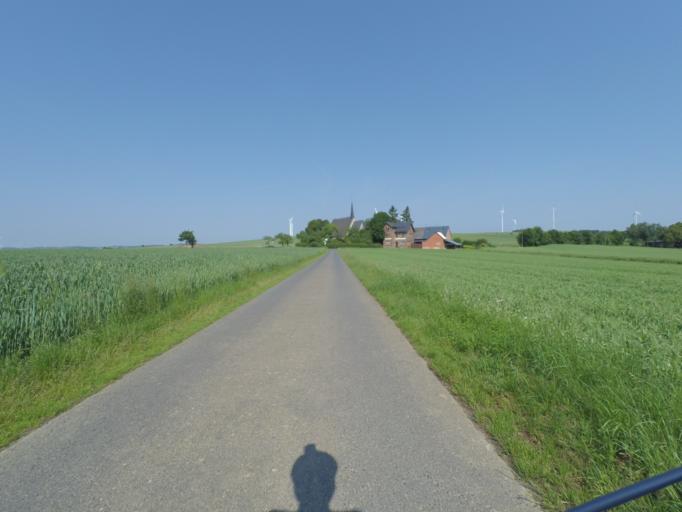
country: DE
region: Rheinland-Pfalz
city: Roes
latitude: 50.2355
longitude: 7.2549
